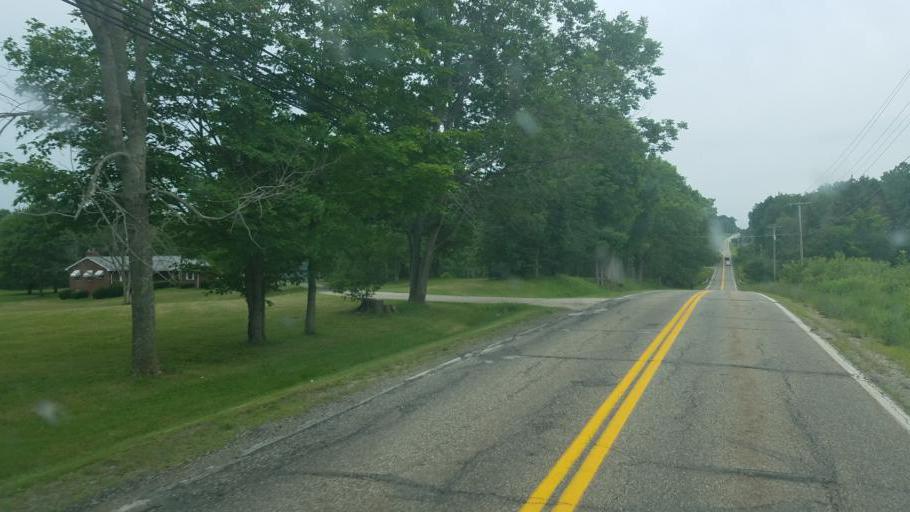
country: US
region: Ohio
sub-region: Portage County
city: Ravenna
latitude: 41.0985
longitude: -81.1853
